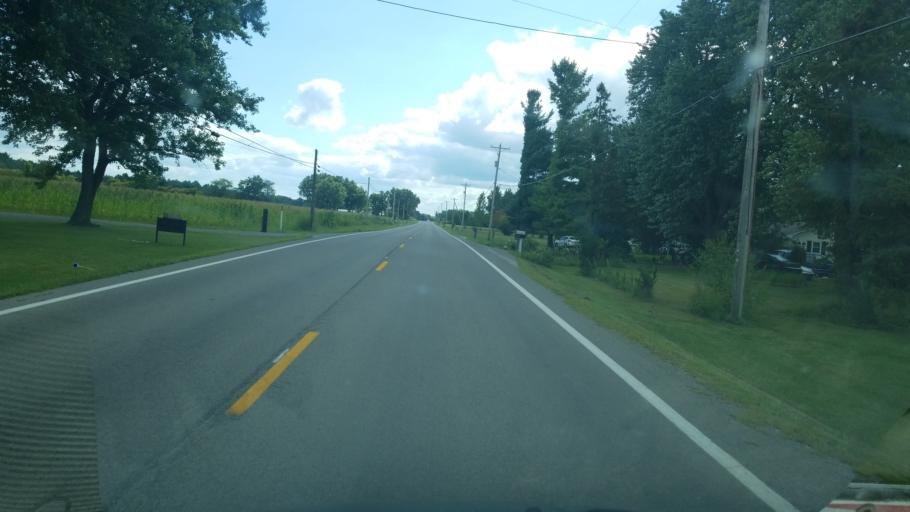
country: US
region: Ohio
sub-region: Allen County
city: Lima
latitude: 40.8139
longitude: -84.0986
